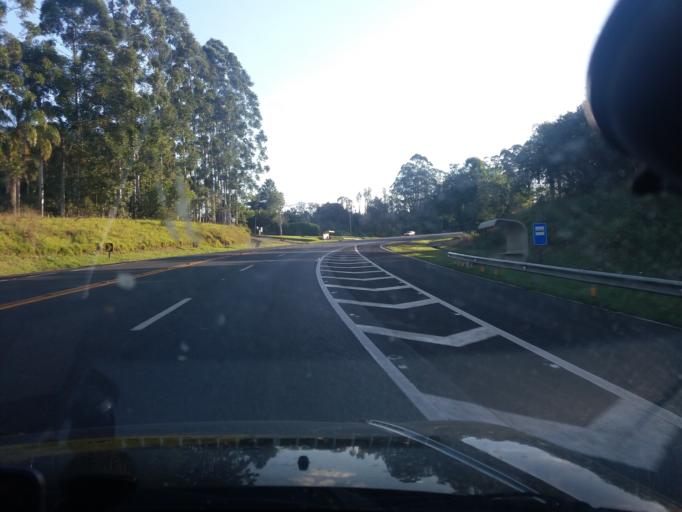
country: BR
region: Sao Paulo
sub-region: Buri
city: Buri
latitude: -23.9291
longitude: -48.6663
